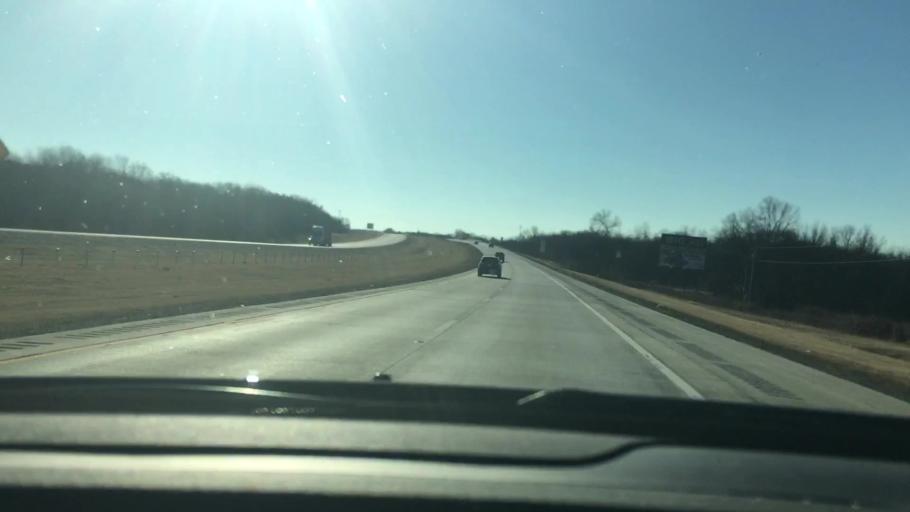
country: US
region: Oklahoma
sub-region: Carter County
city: Ardmore
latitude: 34.1636
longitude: -97.1665
